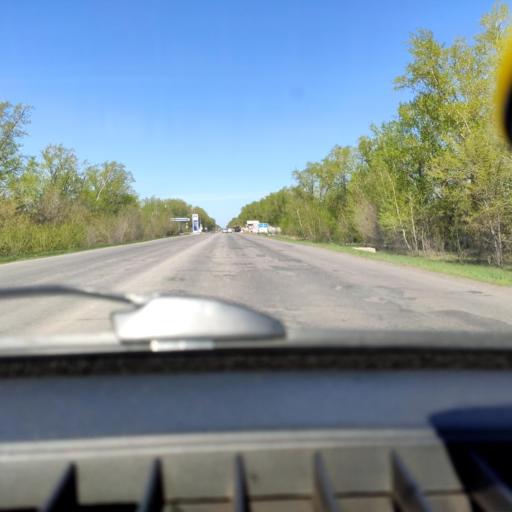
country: RU
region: Samara
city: Tol'yatti
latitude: 53.6184
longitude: 49.4139
